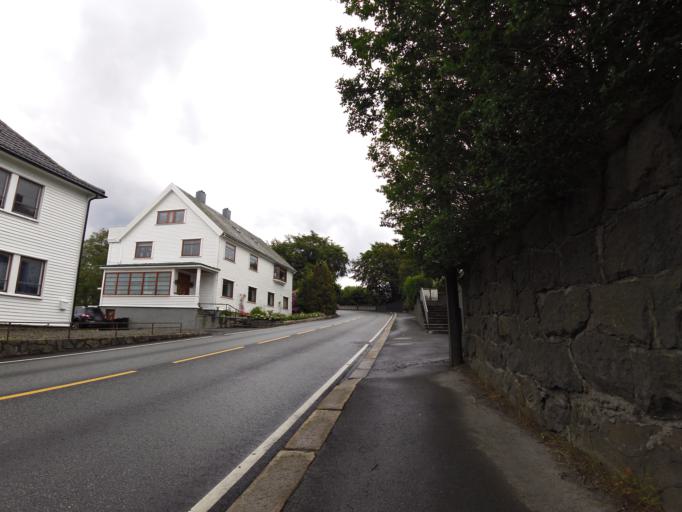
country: NO
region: Vest-Agder
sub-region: Farsund
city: Farsund
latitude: 58.0952
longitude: 6.8097
